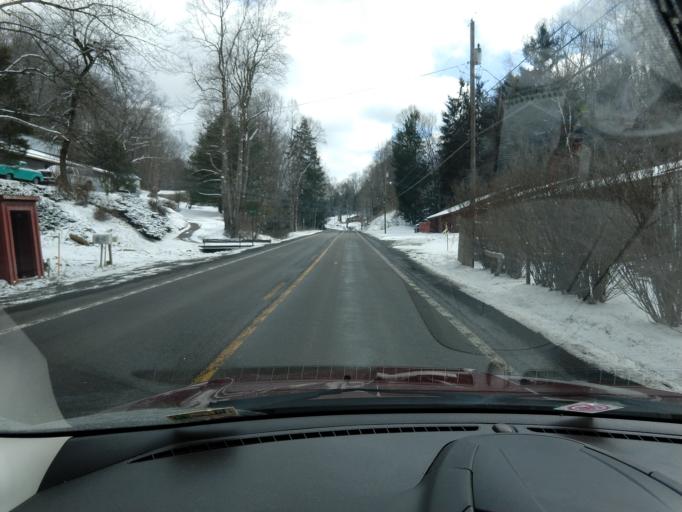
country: US
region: West Virginia
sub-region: Nicholas County
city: Craigsville
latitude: 38.3045
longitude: -80.6515
